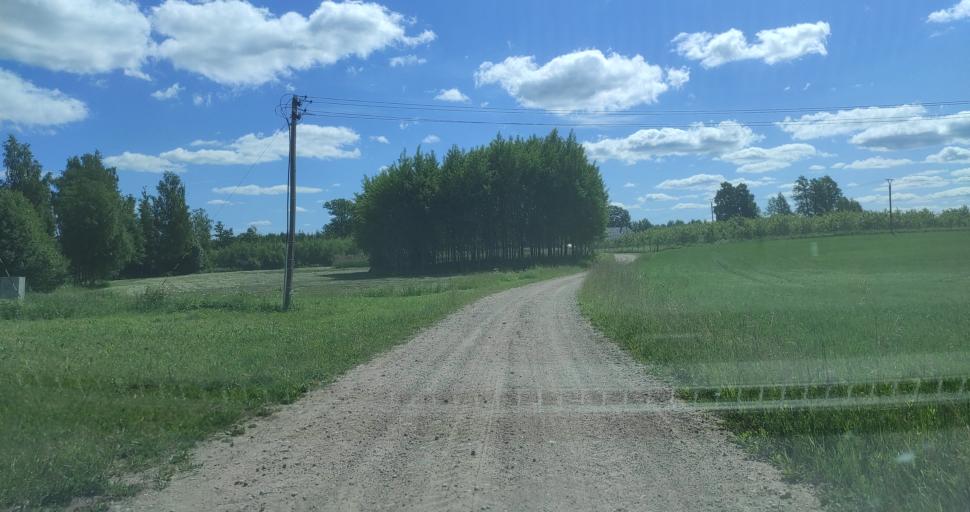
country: LV
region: Alsunga
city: Alsunga
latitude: 56.8706
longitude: 21.7158
